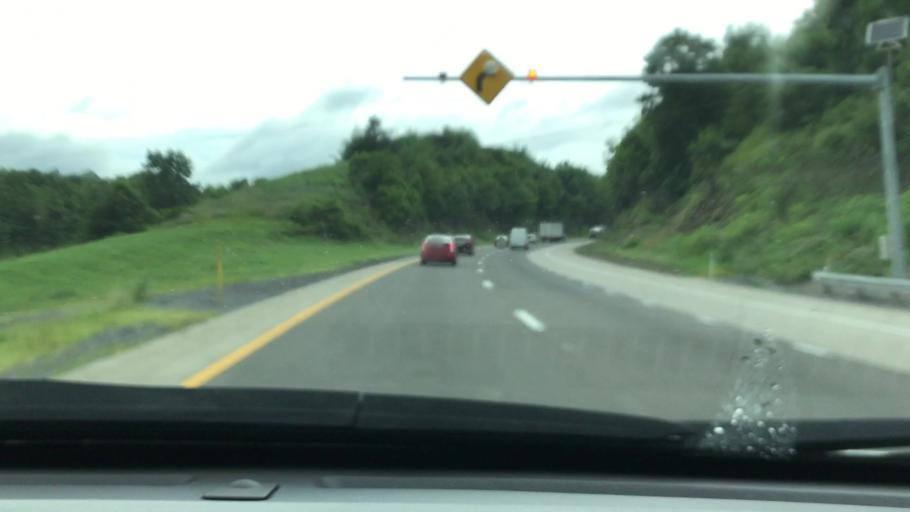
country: US
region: Pennsylvania
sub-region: Clearfield County
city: Clearfield
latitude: 41.0391
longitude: -78.4071
